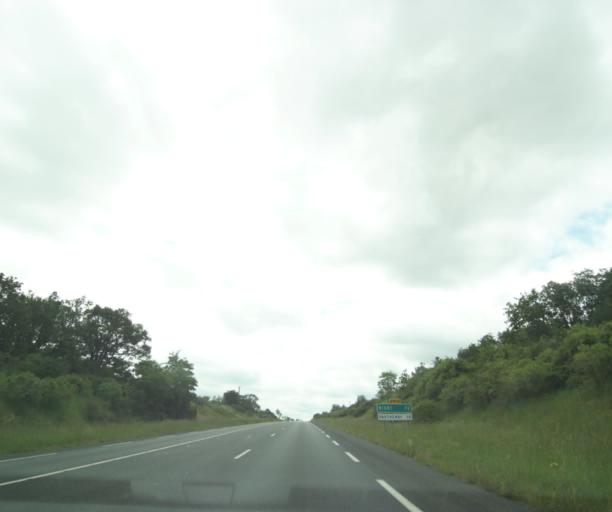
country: FR
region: Poitou-Charentes
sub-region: Departement des Deux-Sevres
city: Saint-Varent
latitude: 46.9108
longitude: -0.1940
